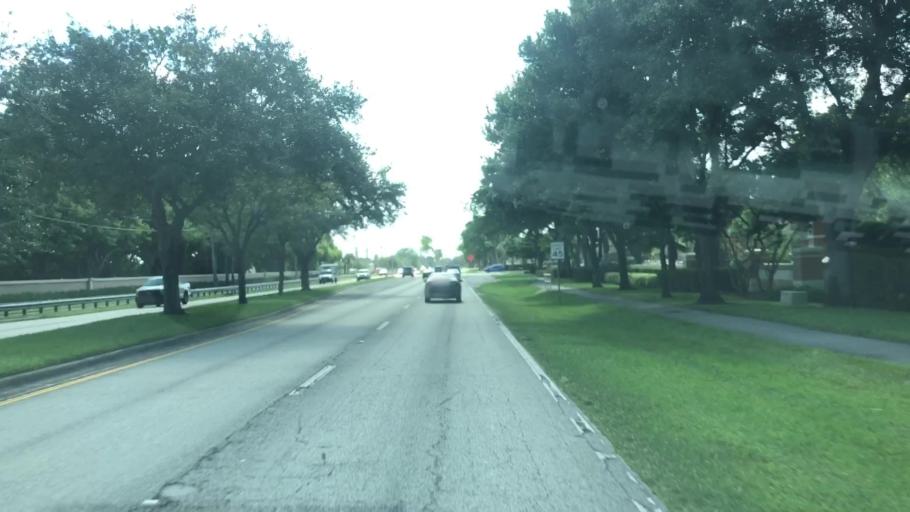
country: US
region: Florida
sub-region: Broward County
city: Parkland
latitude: 26.2869
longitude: -80.2422
